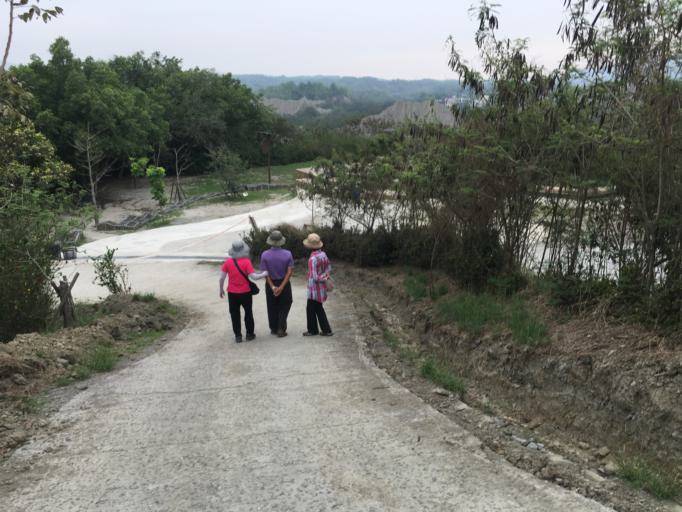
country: TW
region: Taiwan
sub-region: Tainan
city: Tainan
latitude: 22.8885
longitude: 120.3887
